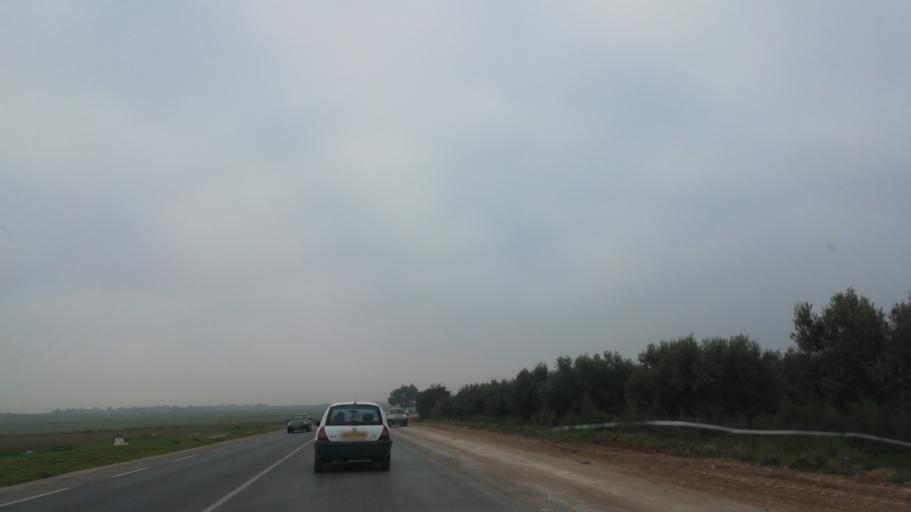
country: DZ
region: Relizane
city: Djidiouia
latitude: 35.9021
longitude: 0.7677
